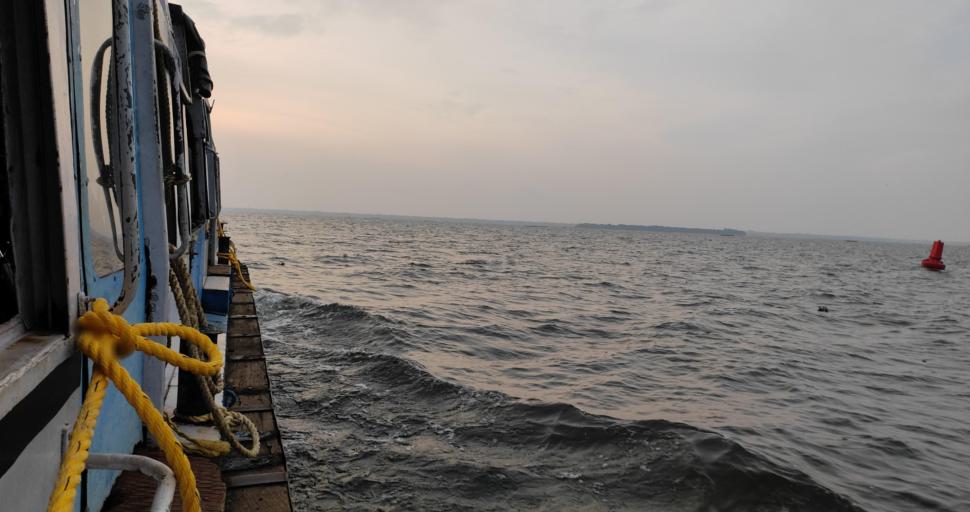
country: IN
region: Kerala
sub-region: Alappuzha
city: Shertallai
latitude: 9.6012
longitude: 76.4057
